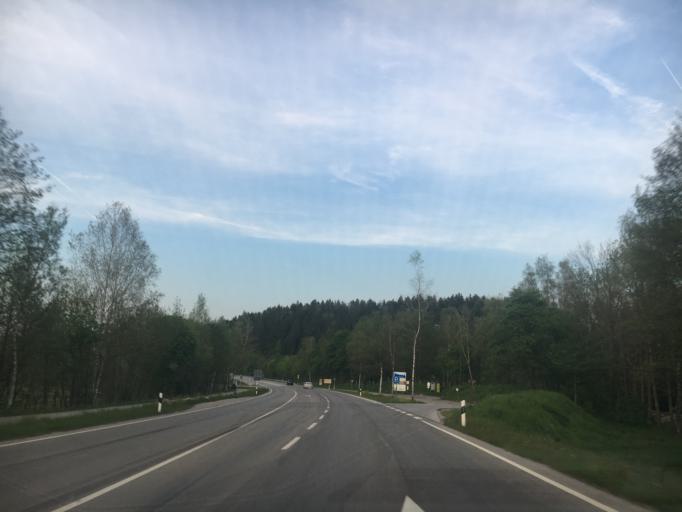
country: DE
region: Bavaria
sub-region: Upper Bavaria
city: Wackersberg
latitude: 47.7511
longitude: 11.5319
